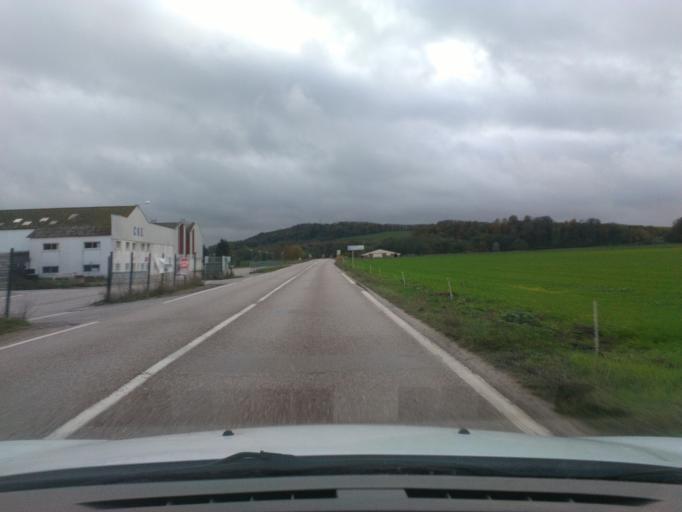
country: FR
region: Lorraine
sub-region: Departement des Vosges
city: Charmes
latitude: 48.3799
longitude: 6.2688
